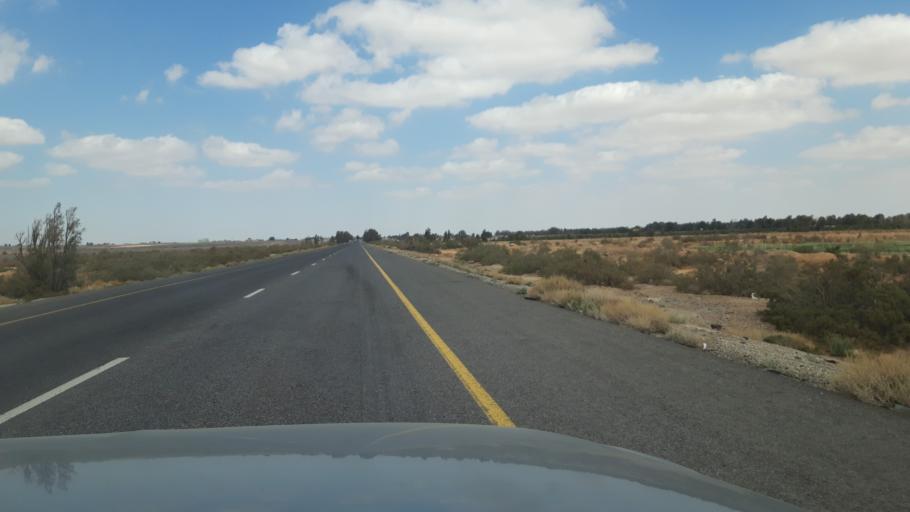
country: JO
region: Amman
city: Al Azraq ash Shamali
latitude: 31.8150
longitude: 36.8030
